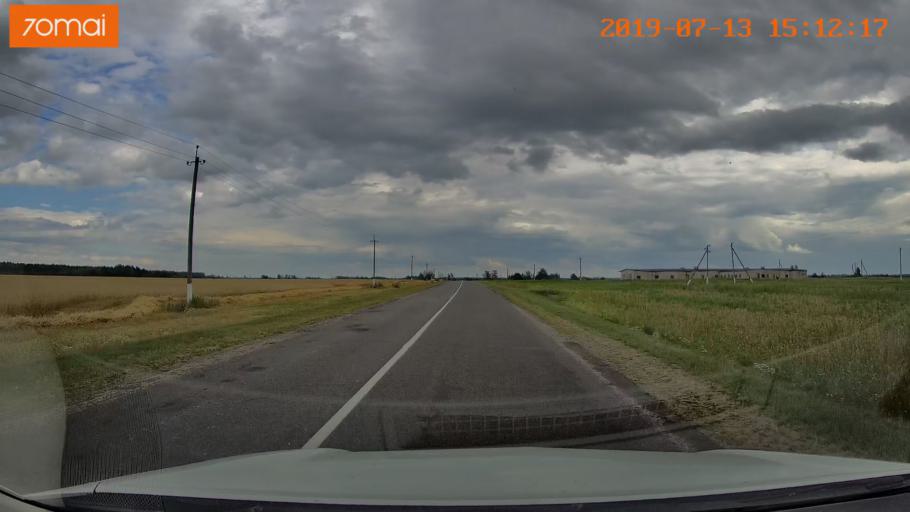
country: BY
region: Mogilev
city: Hlusha
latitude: 53.1512
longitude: 28.7889
